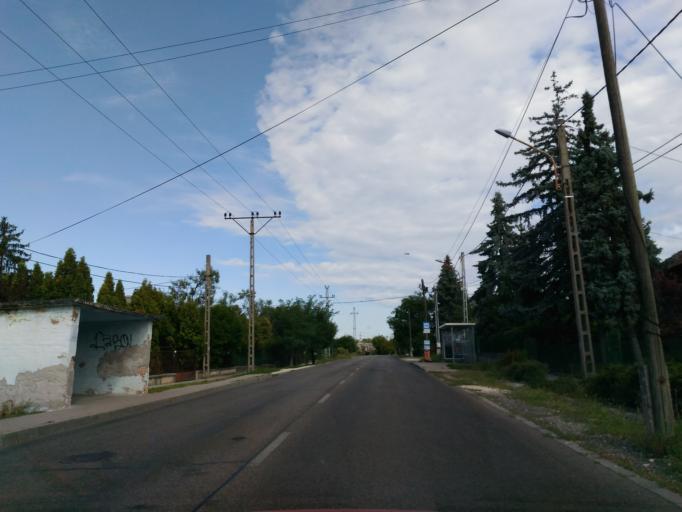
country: HU
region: Pest
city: Diosd
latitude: 47.4090
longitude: 18.9963
